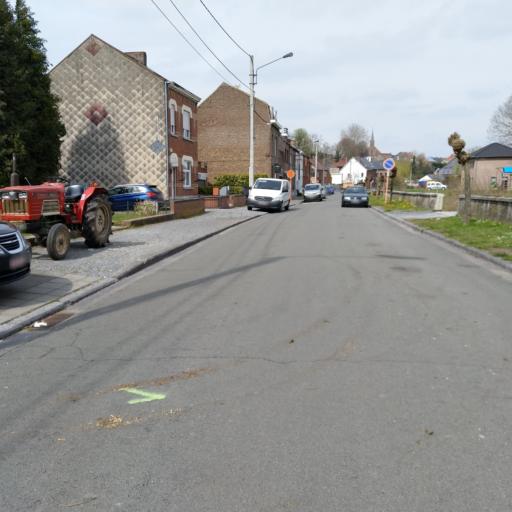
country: BE
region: Wallonia
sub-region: Province du Hainaut
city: Chasse Royale
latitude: 50.4161
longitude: 3.9443
